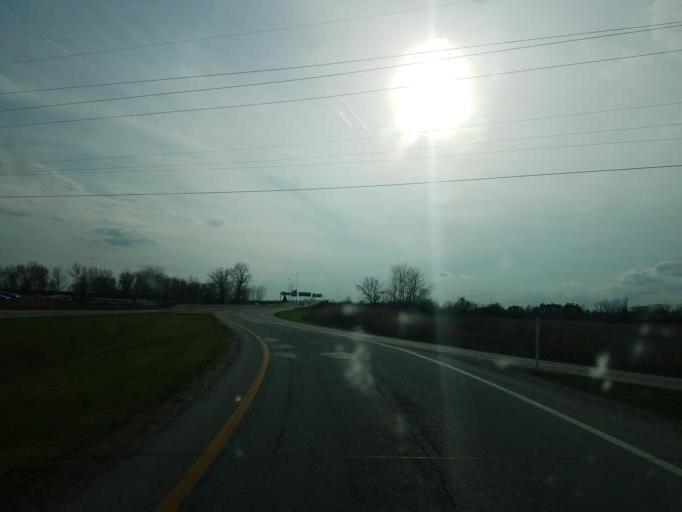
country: US
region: Ohio
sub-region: Ottawa County
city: Port Clinton
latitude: 41.5057
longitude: -82.8304
